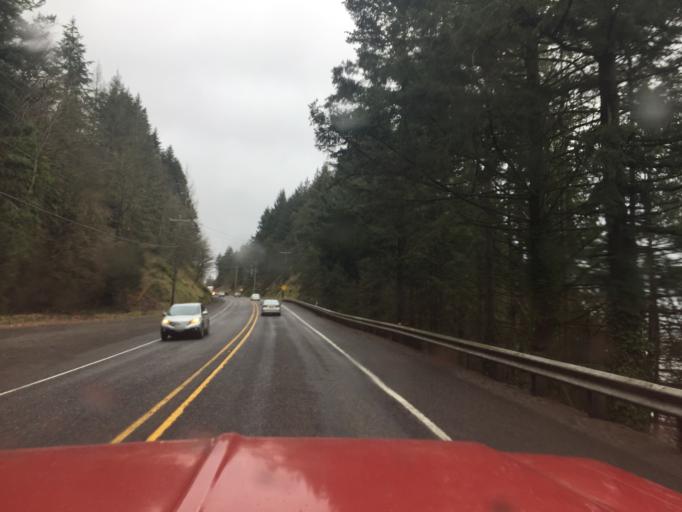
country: US
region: Oregon
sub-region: Columbia County
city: Rainier
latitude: 46.0596
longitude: -122.8951
